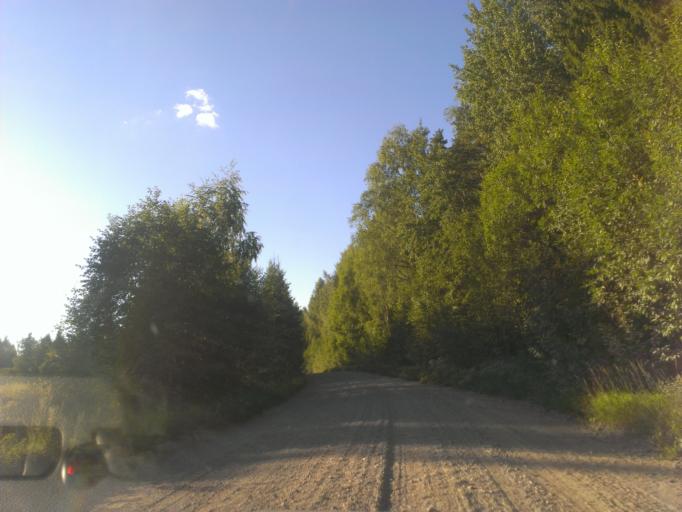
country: LV
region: Malpils
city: Malpils
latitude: 57.0963
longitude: 25.0469
